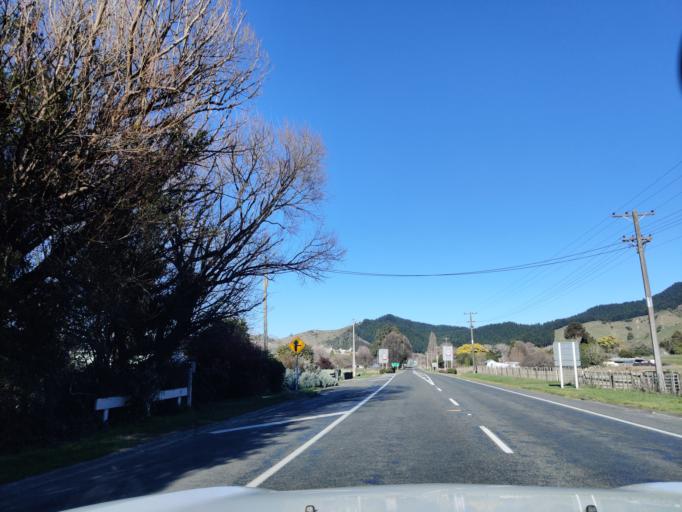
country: NZ
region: Manawatu-Wanganui
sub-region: Ruapehu District
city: Waiouru
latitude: -39.8113
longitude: 175.7859
